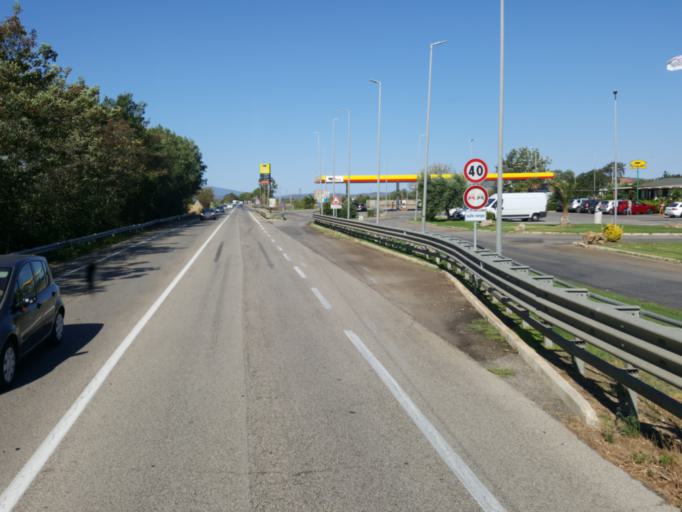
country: IT
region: Tuscany
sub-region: Provincia di Grosseto
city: Capalbio
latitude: 42.4146
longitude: 11.4273
